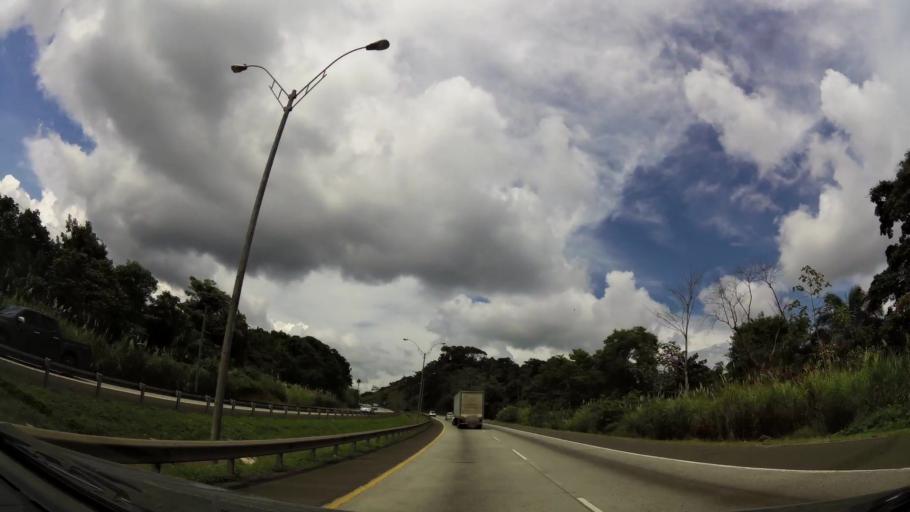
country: PA
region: Panama
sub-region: Distrito Arraijan
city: Arraijan
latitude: 8.9914
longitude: -79.6485
